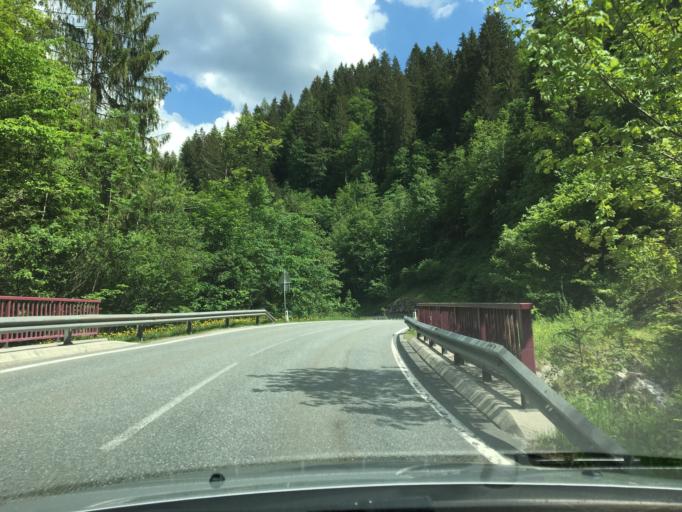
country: AT
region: Salzburg
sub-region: Politischer Bezirk Sankt Johann im Pongau
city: Sankt Johann im Pongau
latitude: 47.3336
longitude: 13.2471
